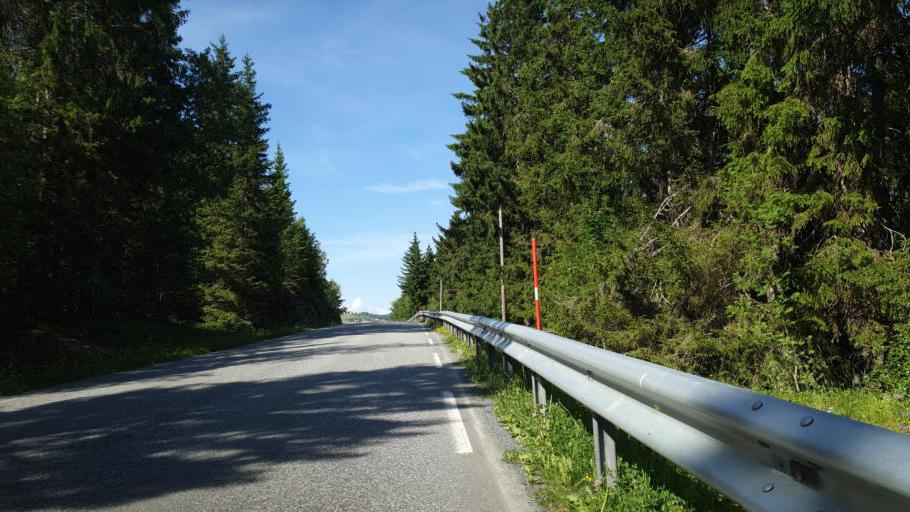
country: NO
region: Nord-Trondelag
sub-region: Leksvik
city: Leksvik
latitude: 63.6552
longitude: 10.6086
